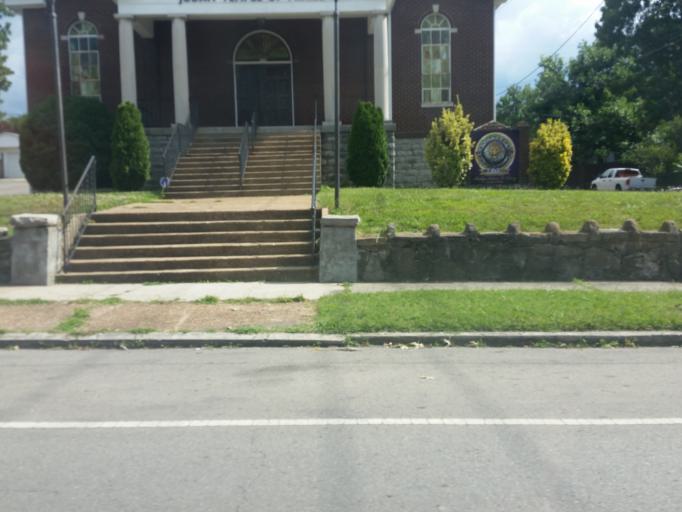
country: US
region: Tennessee
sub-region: Davidson County
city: Nashville
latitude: 36.1702
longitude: -86.7401
